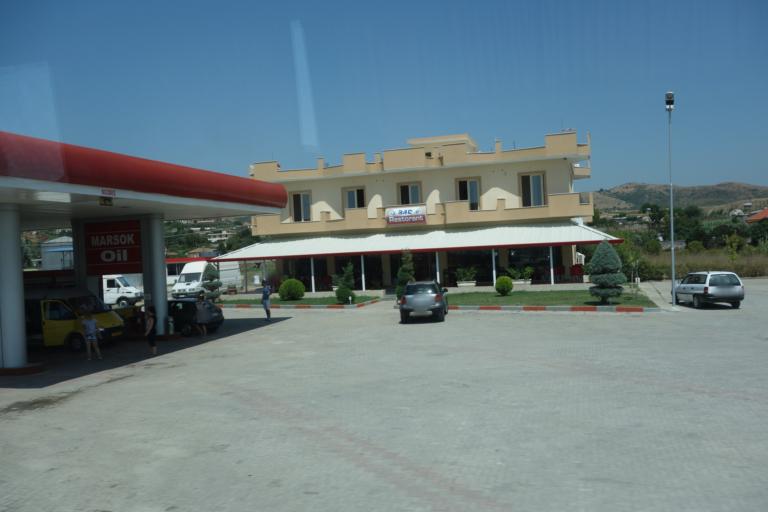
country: AL
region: Tirane
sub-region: Rrethi i Kavajes
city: Gose e Madhe
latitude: 41.0837
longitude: 19.6194
